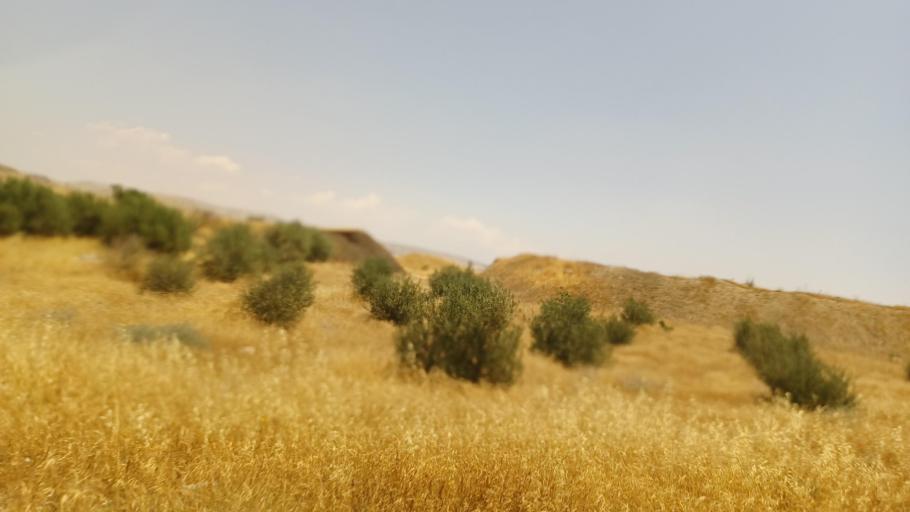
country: CY
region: Larnaka
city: Troulloi
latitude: 35.0114
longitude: 33.6143
